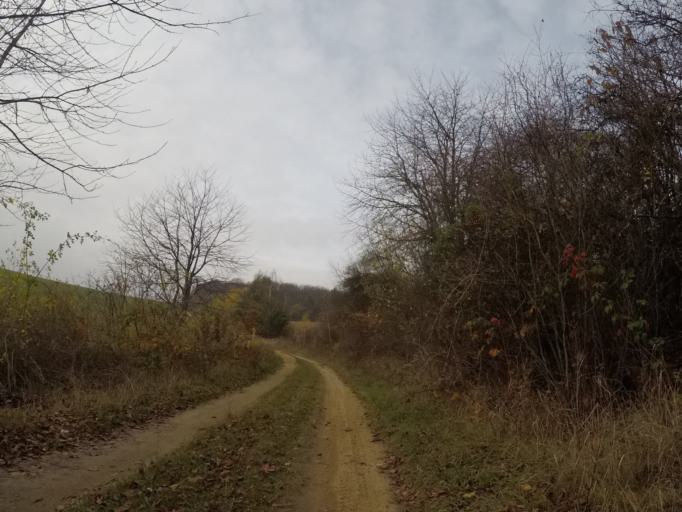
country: SK
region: Presovsky
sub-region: Okres Presov
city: Presov
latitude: 48.9294
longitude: 21.1374
